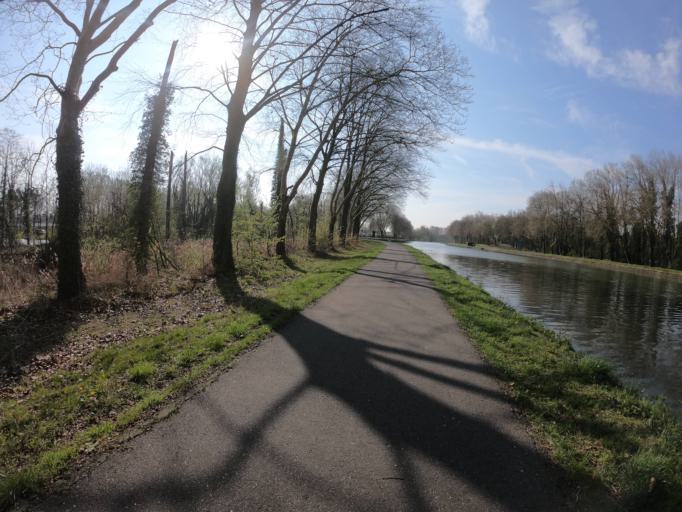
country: BE
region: Flanders
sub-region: Provincie Limburg
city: Kinrooi
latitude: 51.0841
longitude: 5.6980
